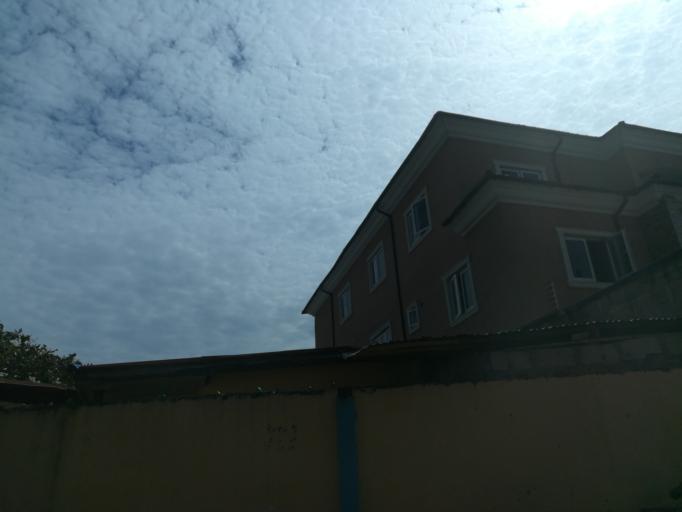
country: NG
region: Lagos
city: Ojota
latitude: 6.5767
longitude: 3.3680
